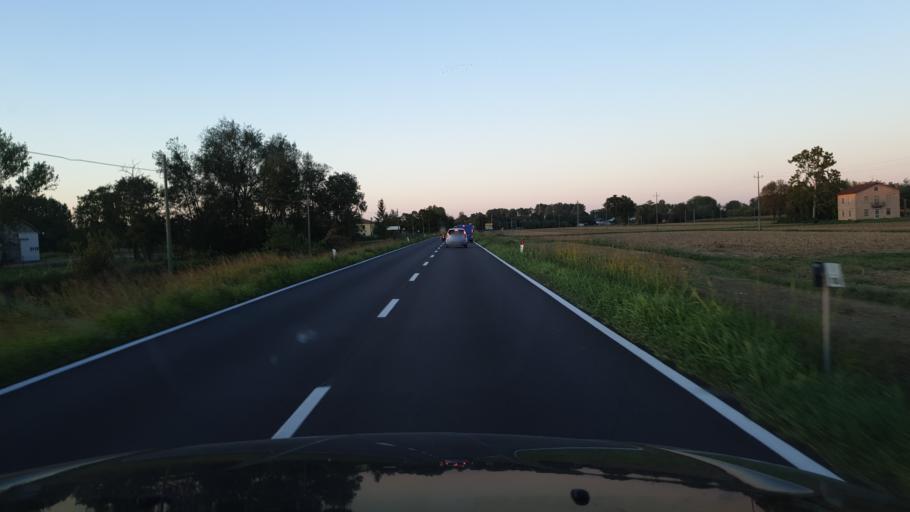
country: IT
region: Emilia-Romagna
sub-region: Provincia di Bologna
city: Ca De Fabbri
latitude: 44.5913
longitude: 11.4327
